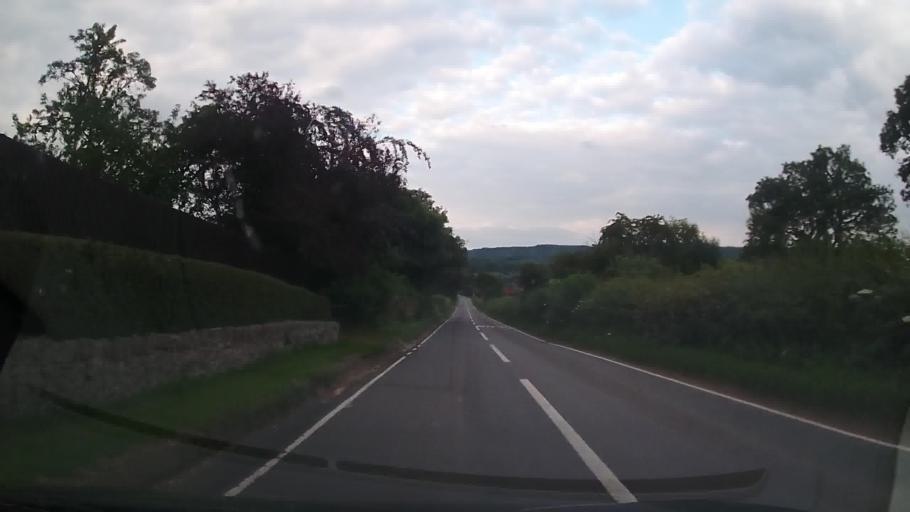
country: GB
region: England
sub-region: Shropshire
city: Pant
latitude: 52.7997
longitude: -3.1208
